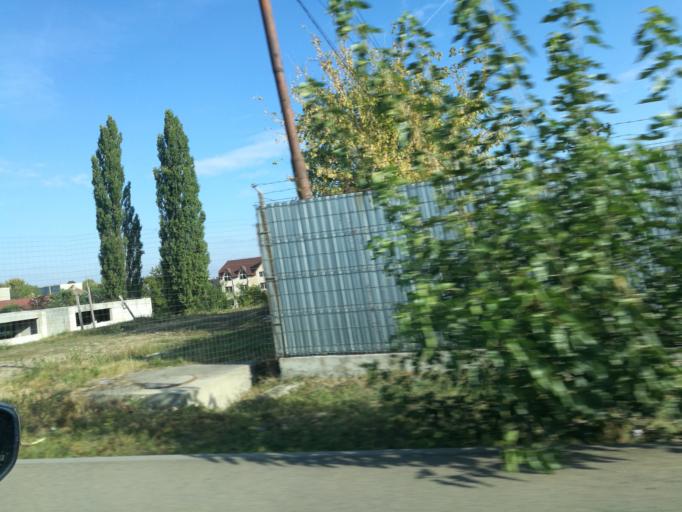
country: RO
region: Bihor
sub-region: Comuna Biharea
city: Oradea
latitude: 47.0395
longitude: 21.9335
